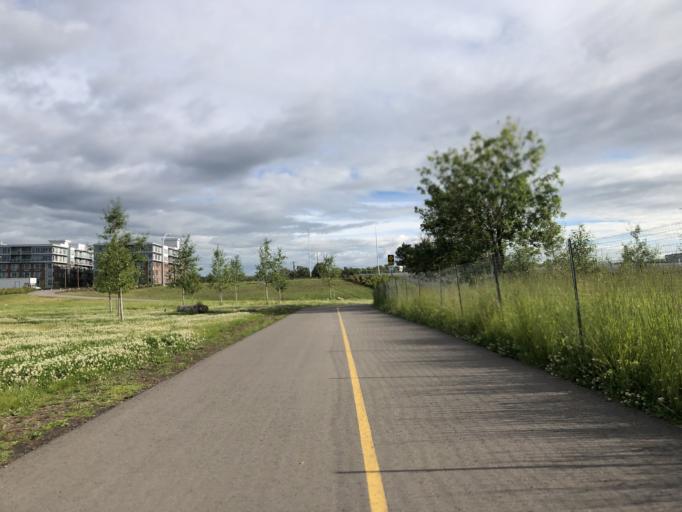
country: CA
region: Alberta
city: Calgary
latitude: 51.0363
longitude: -114.0145
